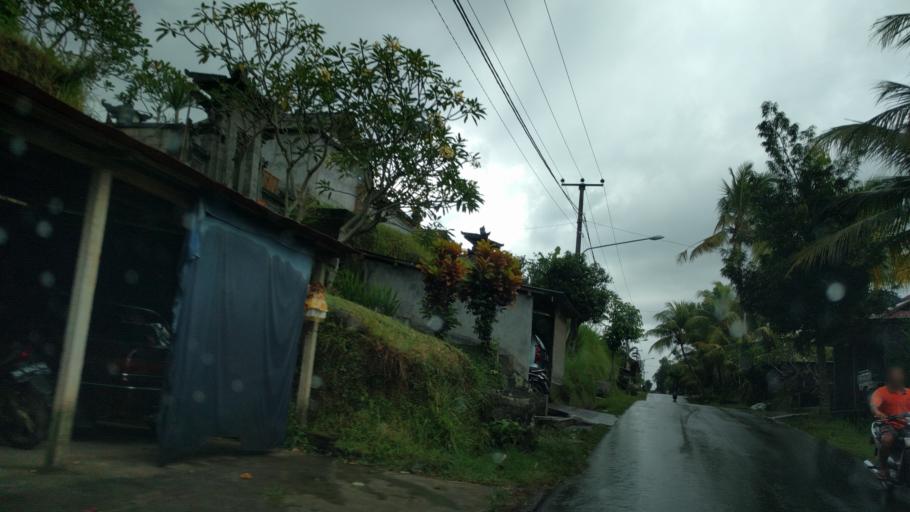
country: ID
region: Bali
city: Bunutan
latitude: -8.4753
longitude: 115.2593
